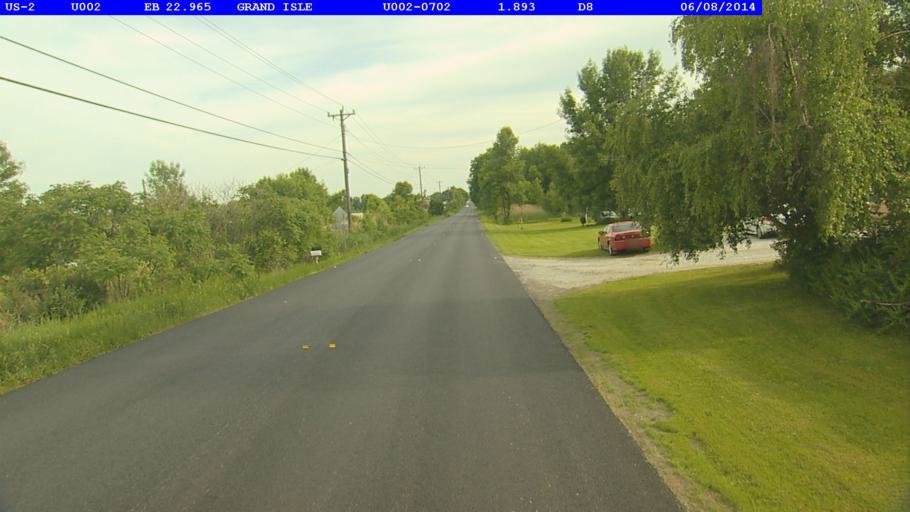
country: US
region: Vermont
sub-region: Grand Isle County
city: North Hero
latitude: 44.7401
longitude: -73.2897
